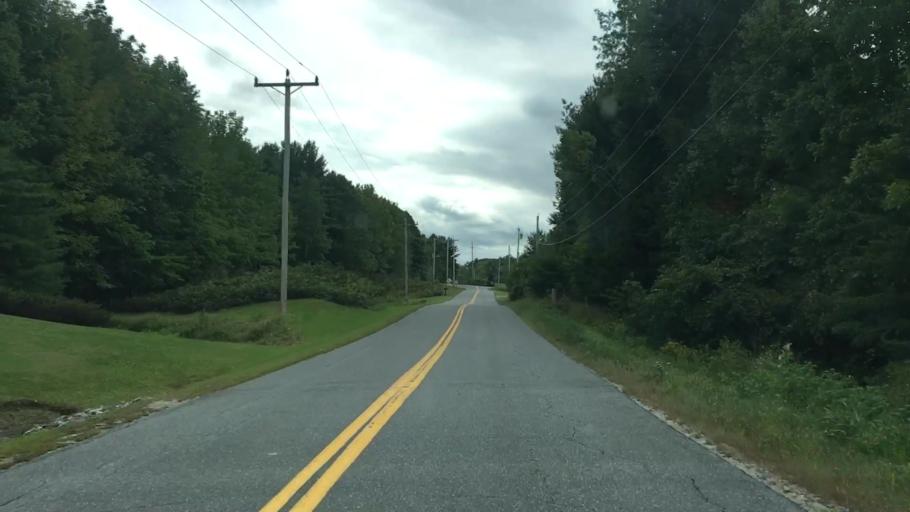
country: US
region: Maine
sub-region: Kennebec County
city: Hallowell
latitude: 44.2674
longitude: -69.8136
